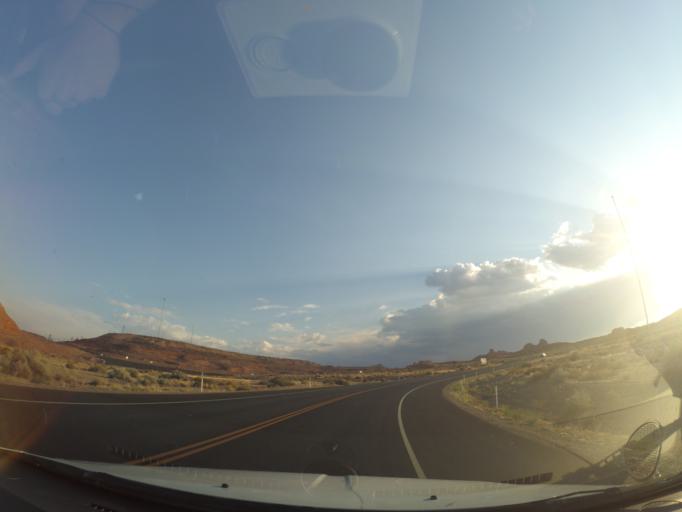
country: US
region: Arizona
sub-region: Coconino County
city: Page
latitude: 36.9406
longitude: -111.4936
